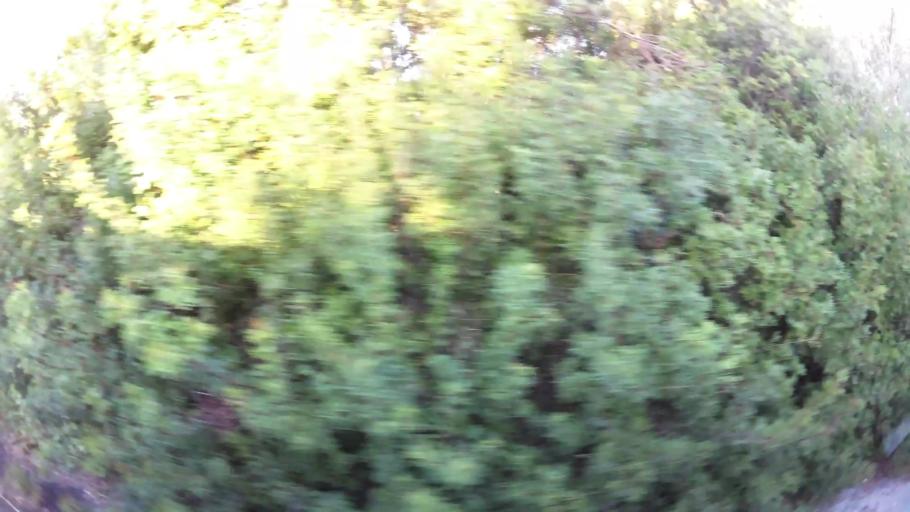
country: GR
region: Attica
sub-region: Nomarchia Anatolikis Attikis
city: Rafina
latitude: 38.0079
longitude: 24.0165
